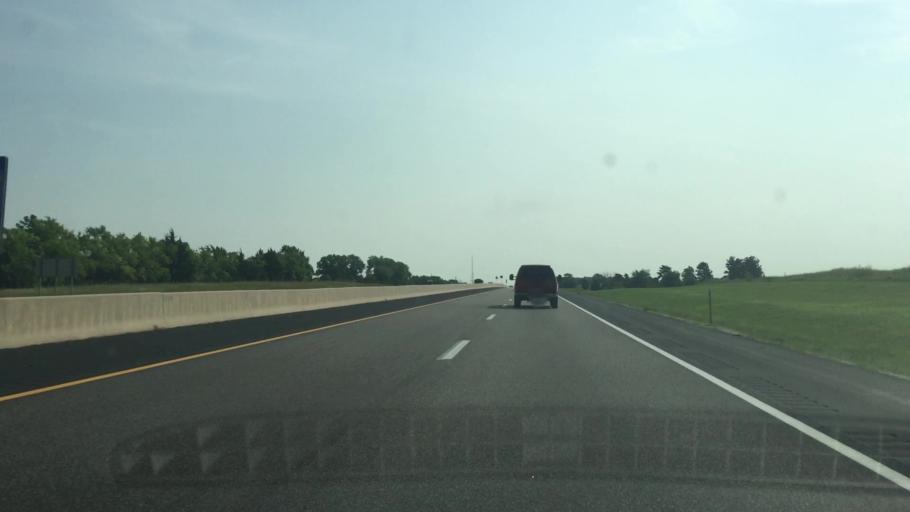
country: US
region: Kansas
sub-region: Butler County
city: Andover
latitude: 37.7028
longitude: -97.1507
